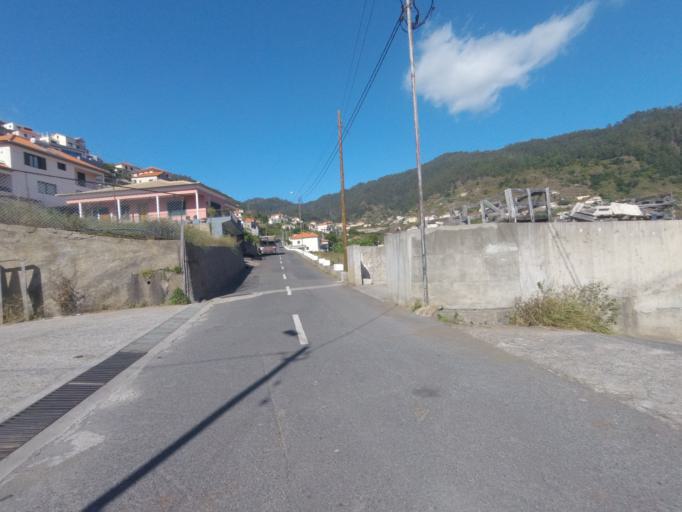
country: PT
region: Madeira
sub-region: Ribeira Brava
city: Campanario
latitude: 32.6747
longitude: -17.0289
